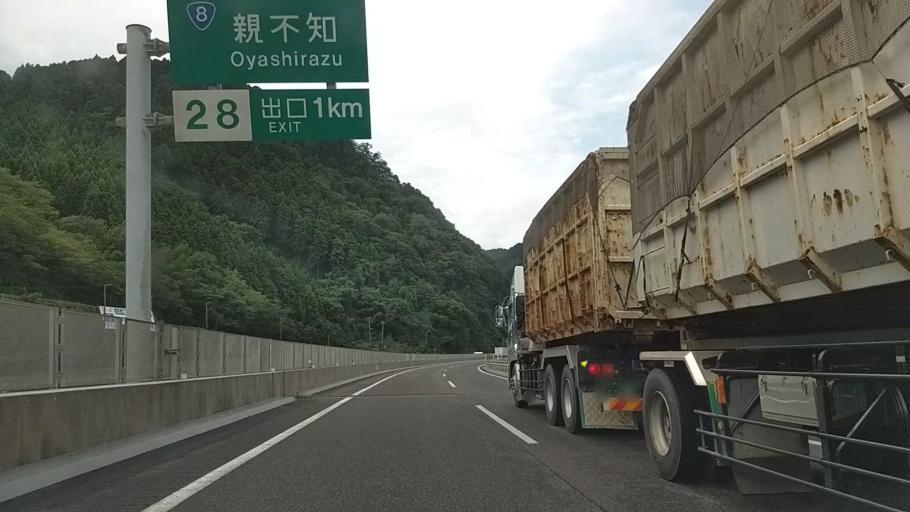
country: JP
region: Niigata
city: Itoigawa
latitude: 37.0045
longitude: 137.7343
